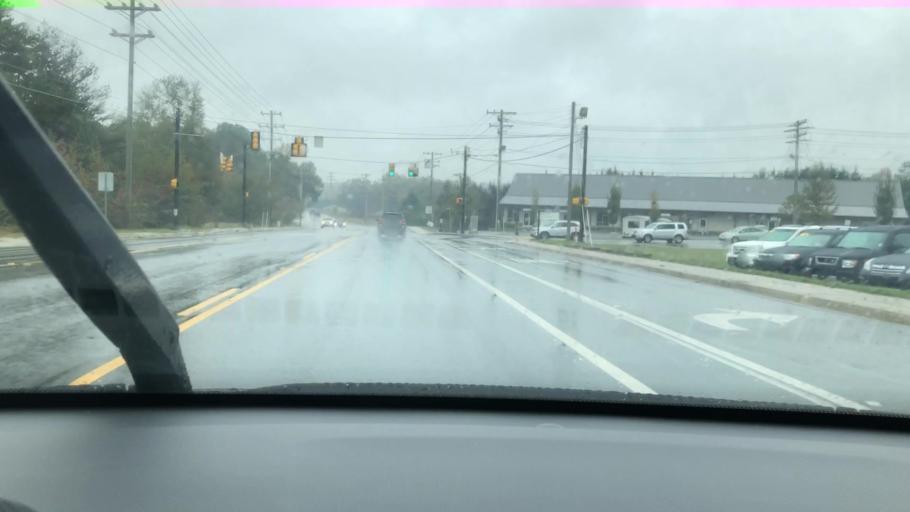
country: US
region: South Carolina
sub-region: Greenville County
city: Five Forks
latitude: 34.8334
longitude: -82.2718
